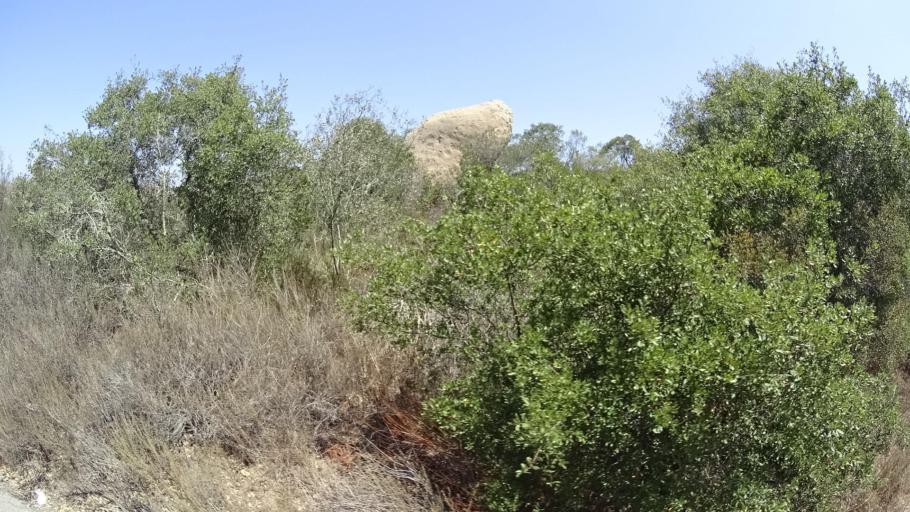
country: US
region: California
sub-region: San Diego County
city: Fallbrook
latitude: 33.4294
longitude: -117.2756
